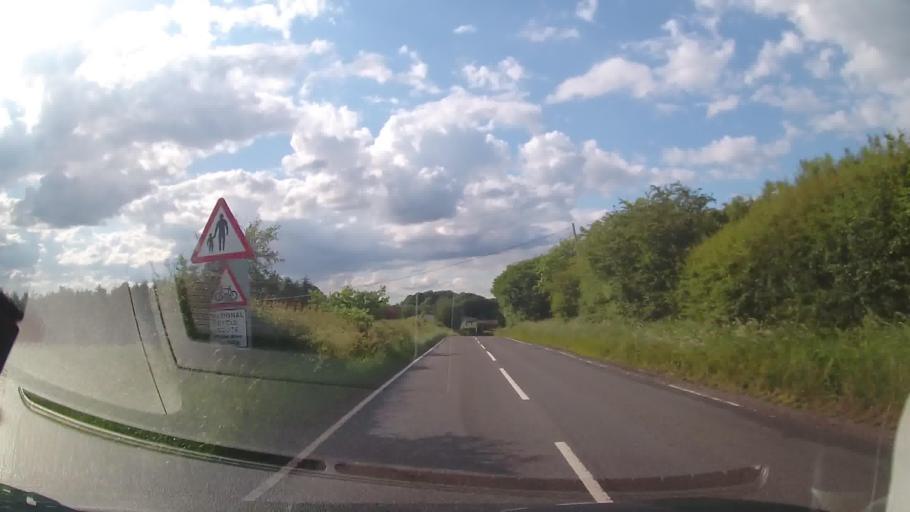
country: GB
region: England
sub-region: Shropshire
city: Harley
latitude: 52.6523
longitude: -2.6085
